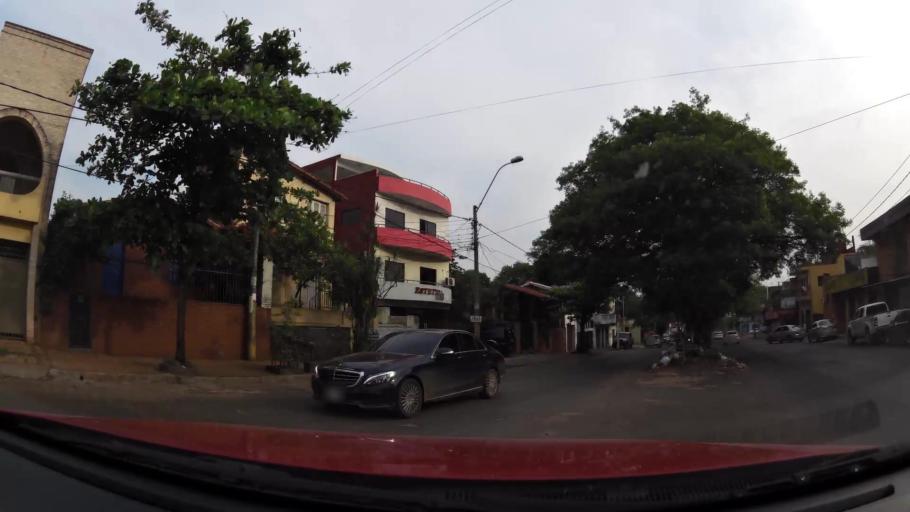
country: PY
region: Asuncion
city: Asuncion
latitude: -25.3121
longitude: -57.6109
